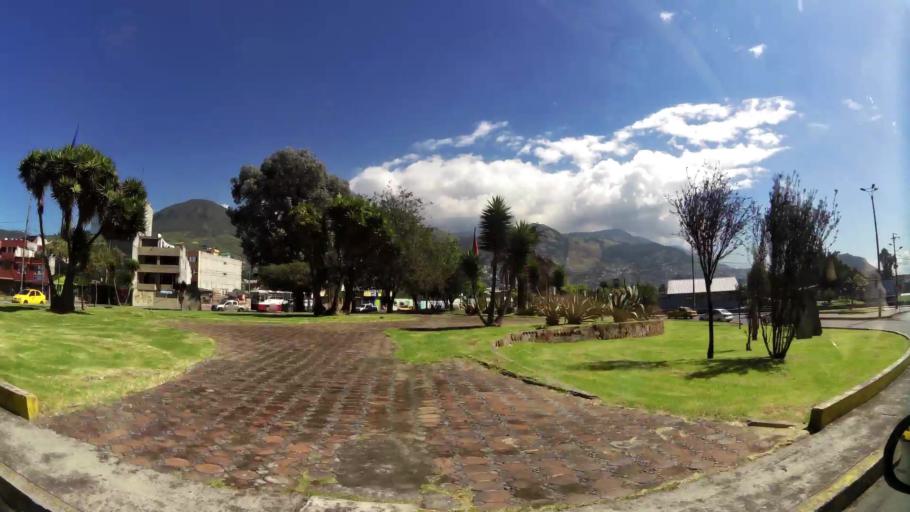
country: EC
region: Pichincha
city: Quito
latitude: -0.2545
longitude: -78.5308
